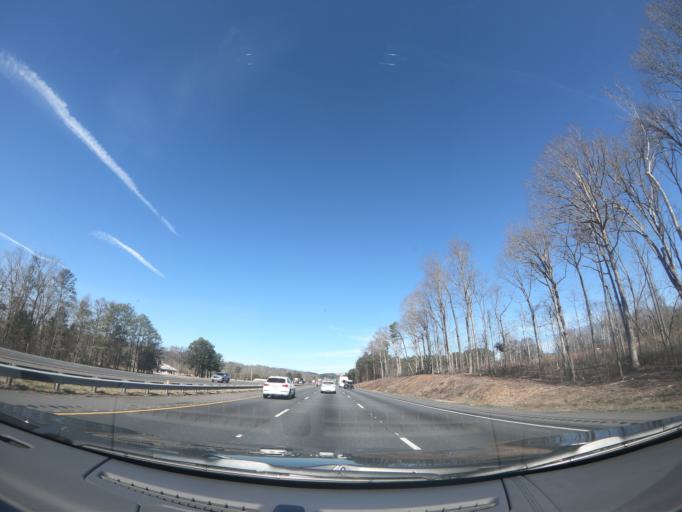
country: US
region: Georgia
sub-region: Catoosa County
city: Indian Springs
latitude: 34.9475
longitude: -85.1739
